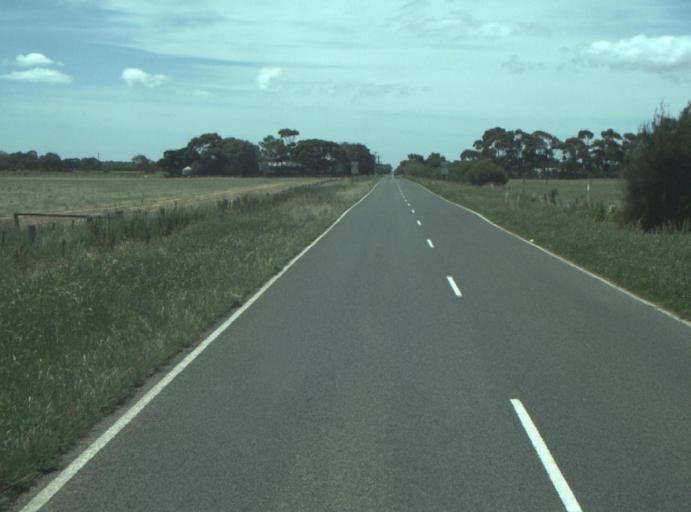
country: AU
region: Victoria
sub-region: Greater Geelong
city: Lara
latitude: -38.0061
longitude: 144.3748
